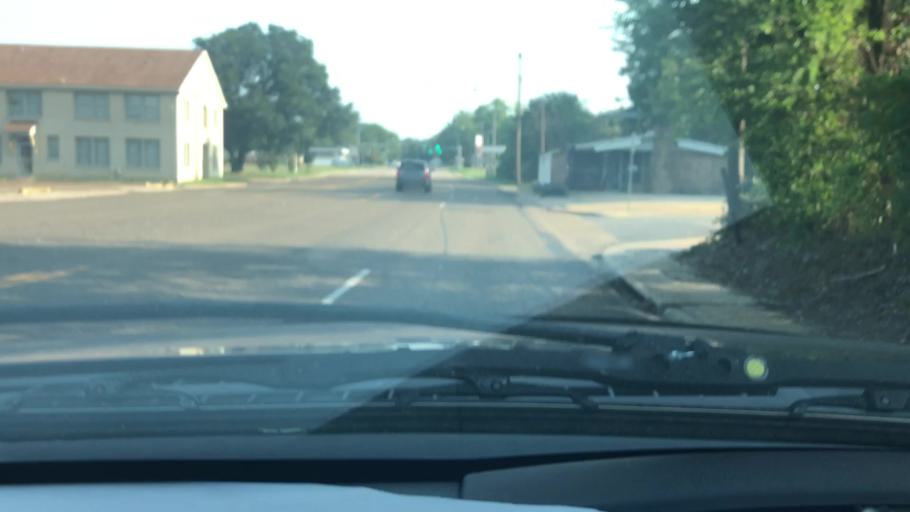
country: US
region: Texas
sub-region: Bowie County
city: Texarkana
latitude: 33.4212
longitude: -94.0610
